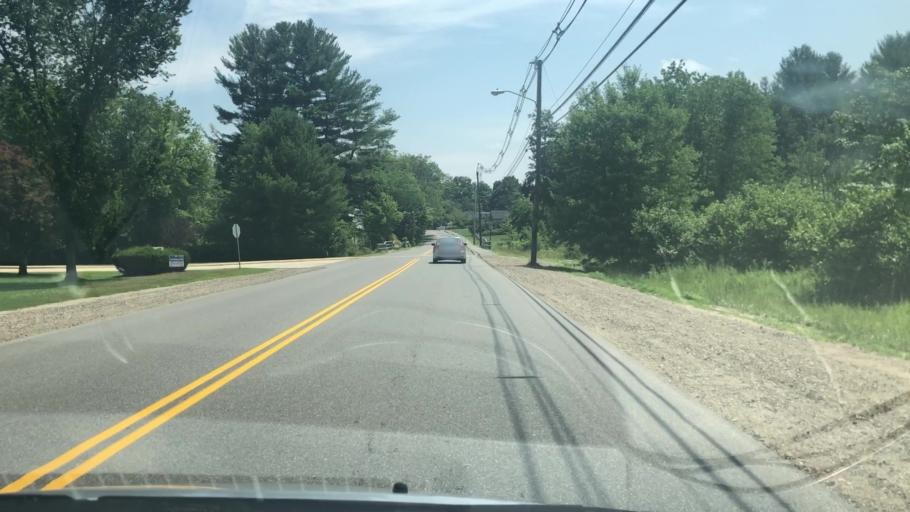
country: US
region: New Hampshire
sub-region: Hillsborough County
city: Milford
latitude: 42.8675
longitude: -71.6318
